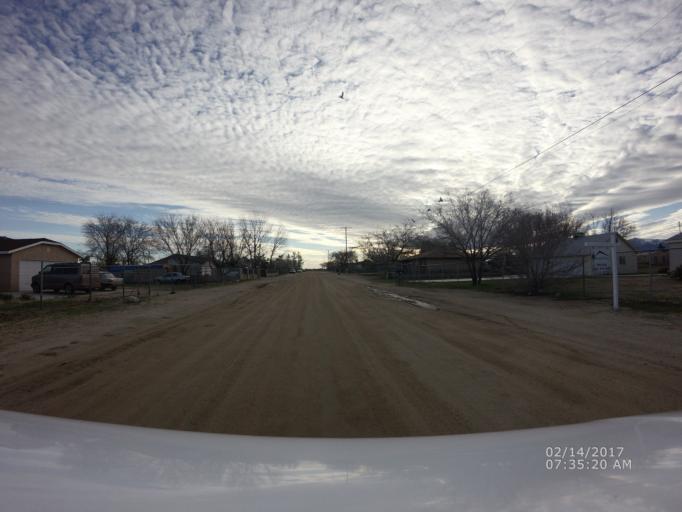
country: US
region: California
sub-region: Los Angeles County
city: Littlerock
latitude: 34.5466
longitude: -117.9431
